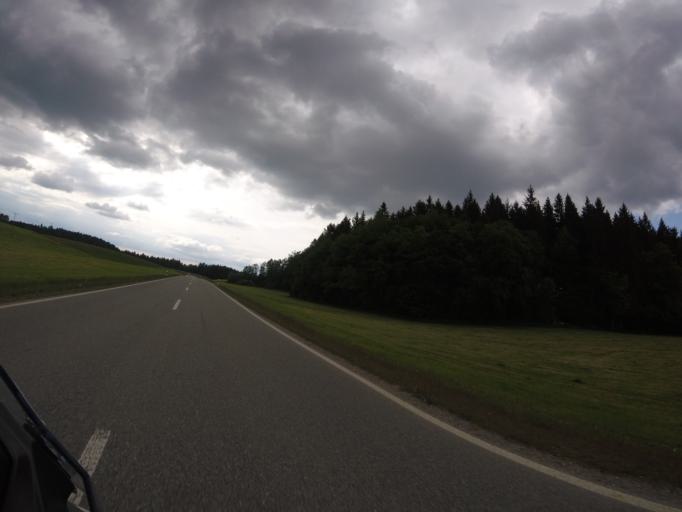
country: DE
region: Bavaria
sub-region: Upper Bavaria
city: Dietramszell
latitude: 47.8590
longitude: 11.5748
